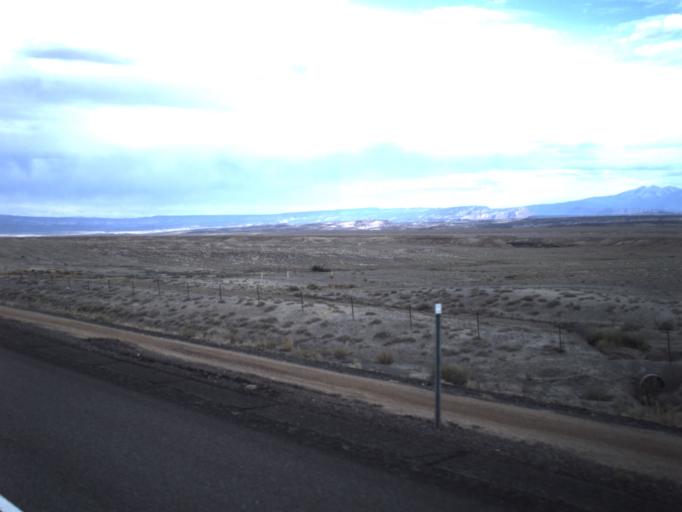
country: US
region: Utah
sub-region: Grand County
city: Moab
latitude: 38.9362
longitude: -109.4772
